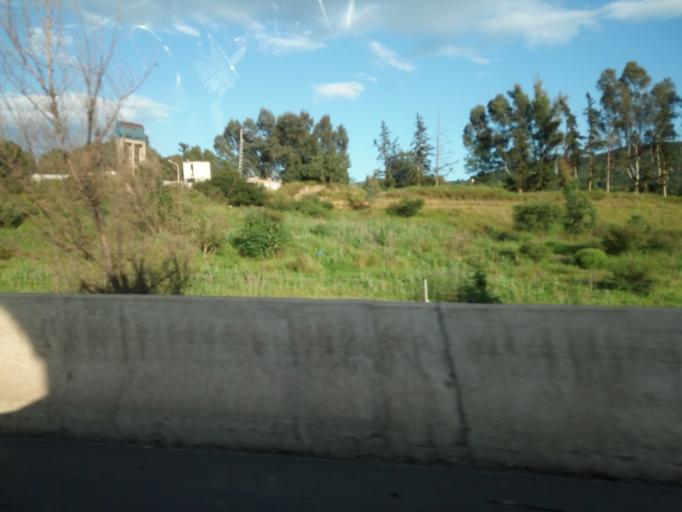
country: DZ
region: Tipaza
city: El Affroun
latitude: 36.4412
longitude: 2.5803
